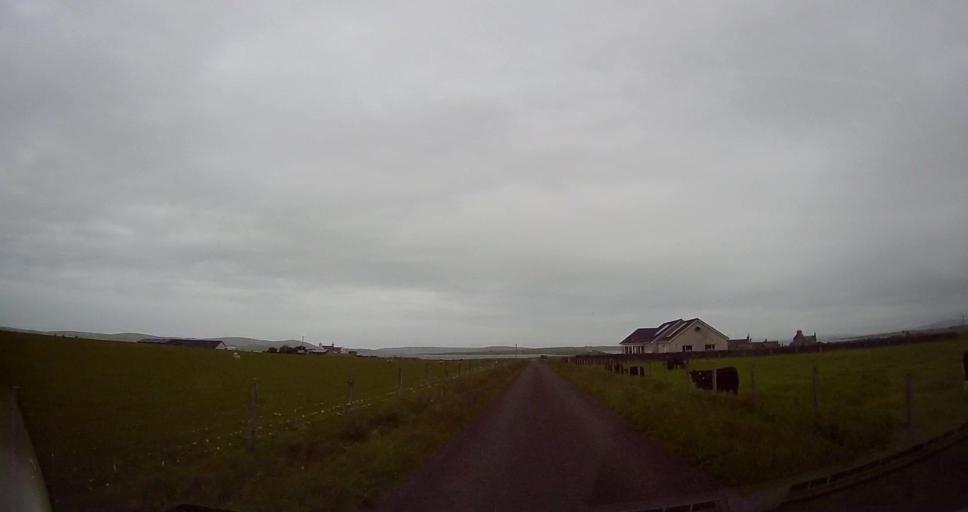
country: GB
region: Scotland
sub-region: Orkney Islands
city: Stromness
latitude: 58.9877
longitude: -3.1952
